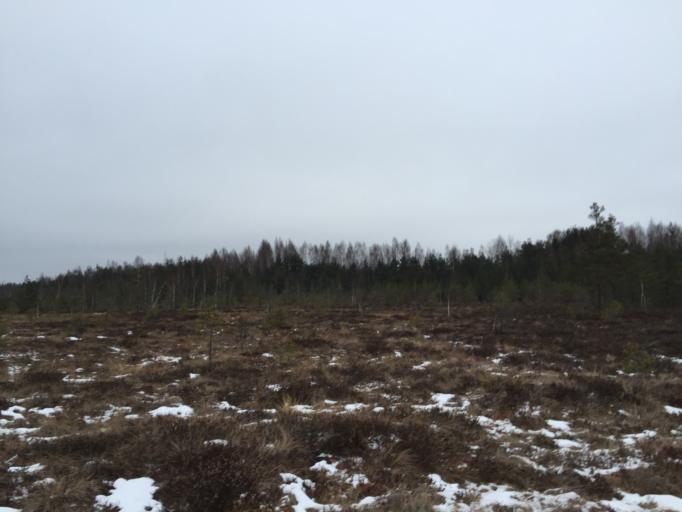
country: LV
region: Saulkrastu
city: Saulkrasti
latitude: 57.2362
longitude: 24.5067
